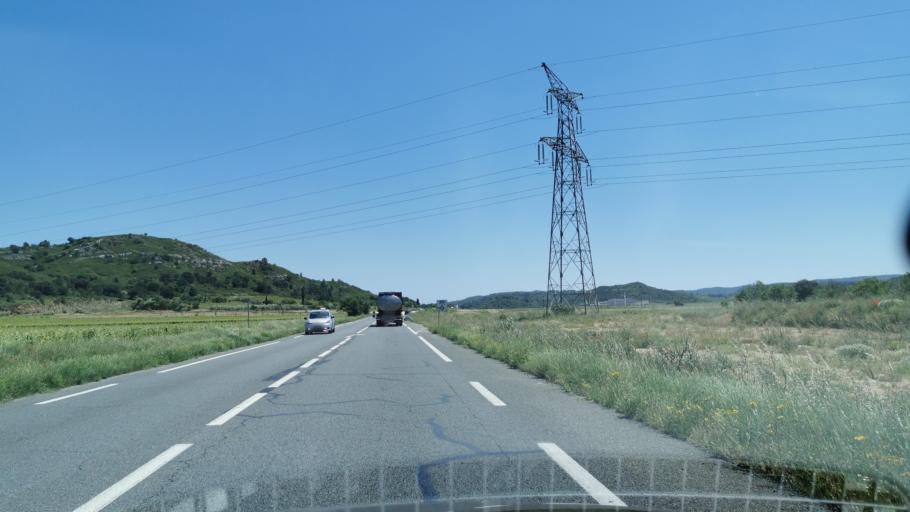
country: FR
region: Languedoc-Roussillon
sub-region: Departement de l'Aude
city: Nevian
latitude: 43.2000
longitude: 2.8954
